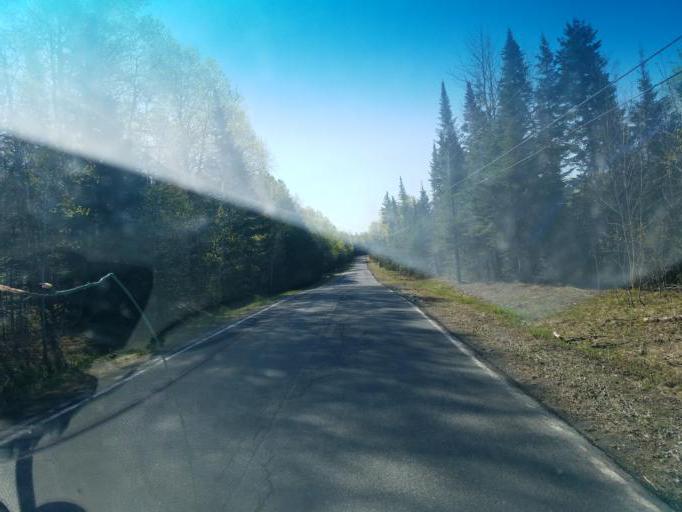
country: US
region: Maine
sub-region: Aroostook County
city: Caribou
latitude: 46.8527
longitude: -68.2011
